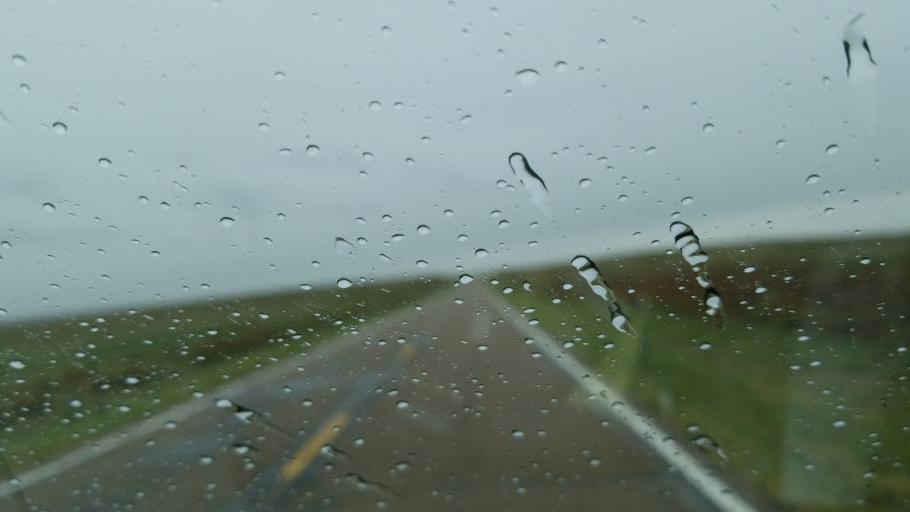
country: US
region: Colorado
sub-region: Lincoln County
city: Hugo
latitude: 38.8555
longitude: -103.1525
